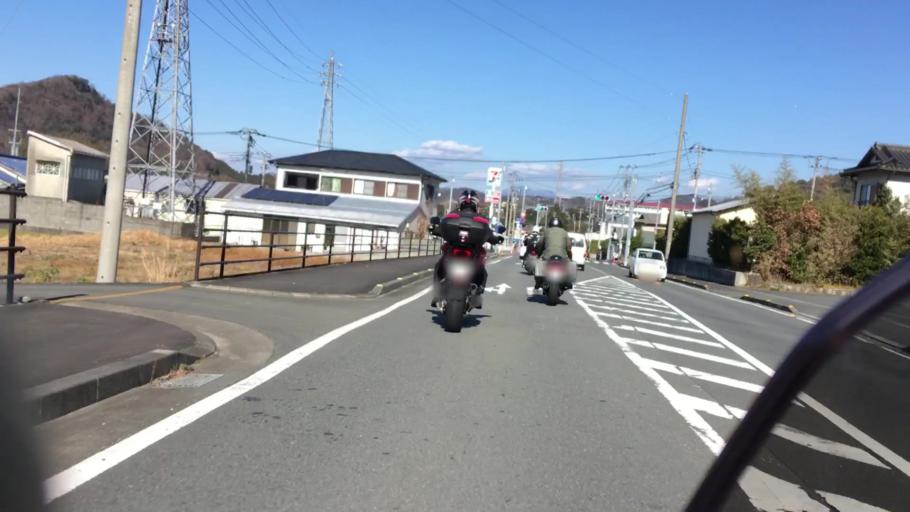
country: JP
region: Shizuoka
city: Ito
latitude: 34.9703
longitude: 138.9491
